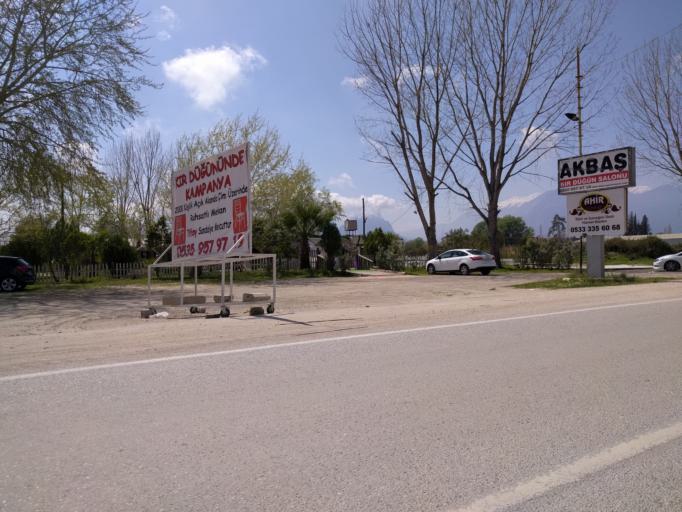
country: TR
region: Antalya
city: Cakirlar
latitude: 36.8968
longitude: 30.6131
